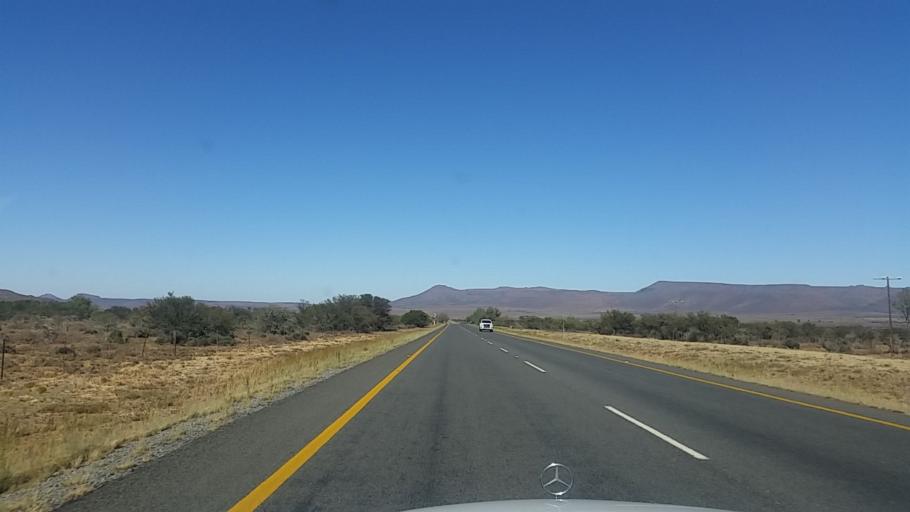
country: ZA
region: Eastern Cape
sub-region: Cacadu District Municipality
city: Graaff-Reinet
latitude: -31.9847
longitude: 24.6936
